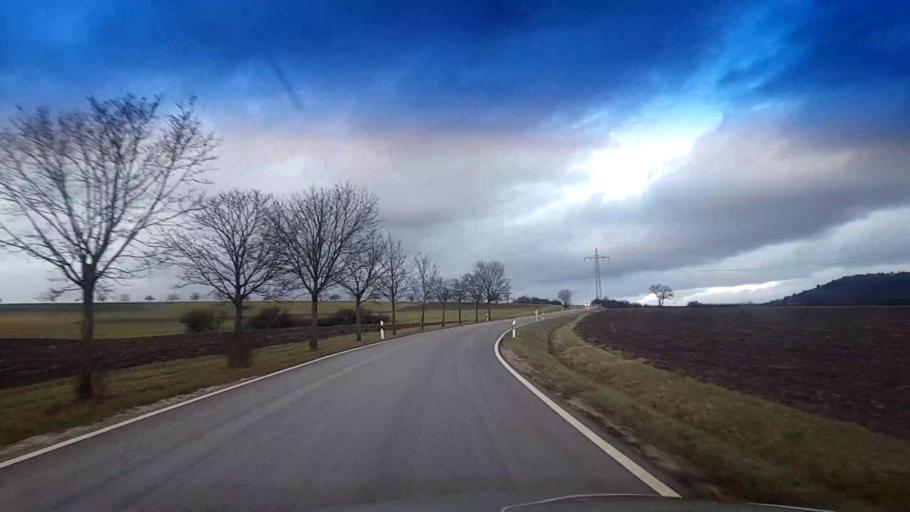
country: DE
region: Bavaria
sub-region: Upper Franconia
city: Strullendorf
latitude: 49.8724
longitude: 11.0035
